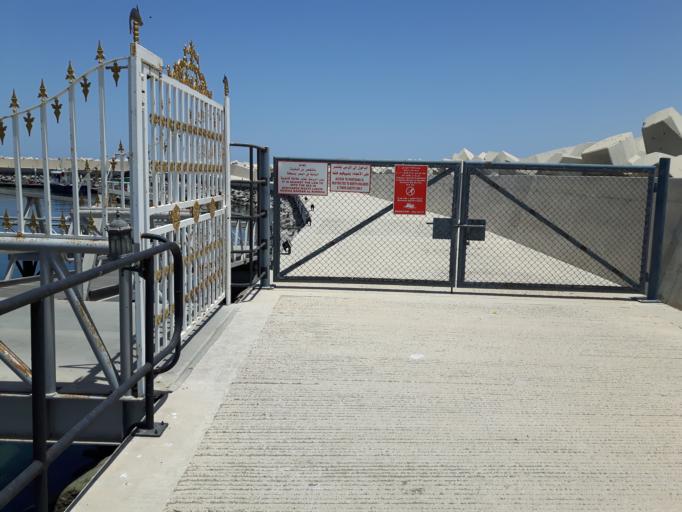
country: OM
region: Muhafazat Masqat
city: Muscat
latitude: 23.5811
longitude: 58.6072
